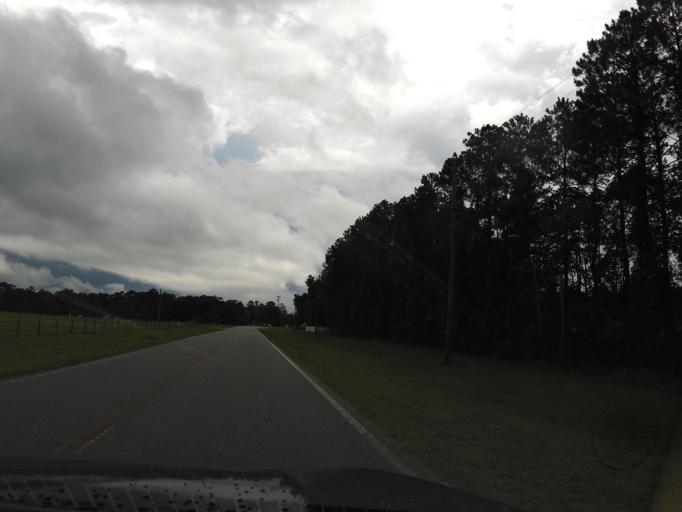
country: US
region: Georgia
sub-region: Camden County
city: Kingsland
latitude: 30.7803
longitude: -81.6489
